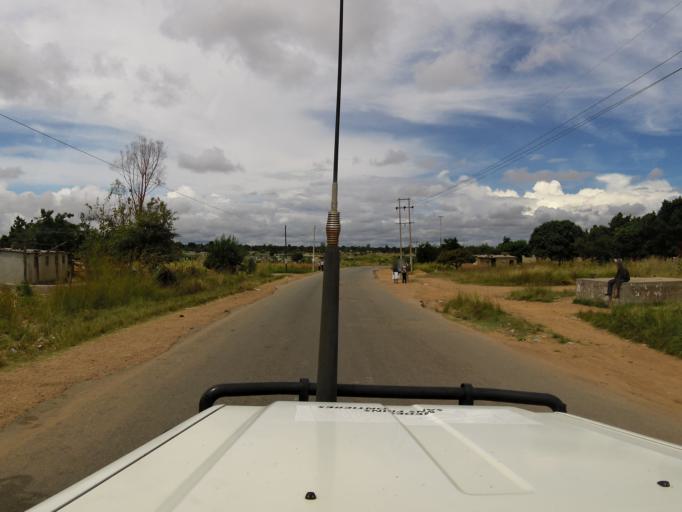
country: ZW
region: Harare
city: Epworth
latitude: -17.8901
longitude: 31.1407
